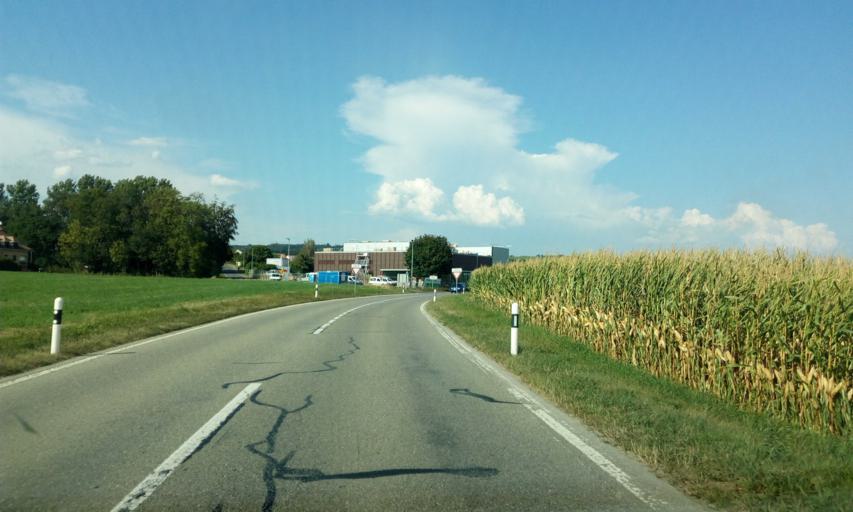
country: CH
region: Fribourg
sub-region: Broye District
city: Domdidier
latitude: 46.8990
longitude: 6.9911
